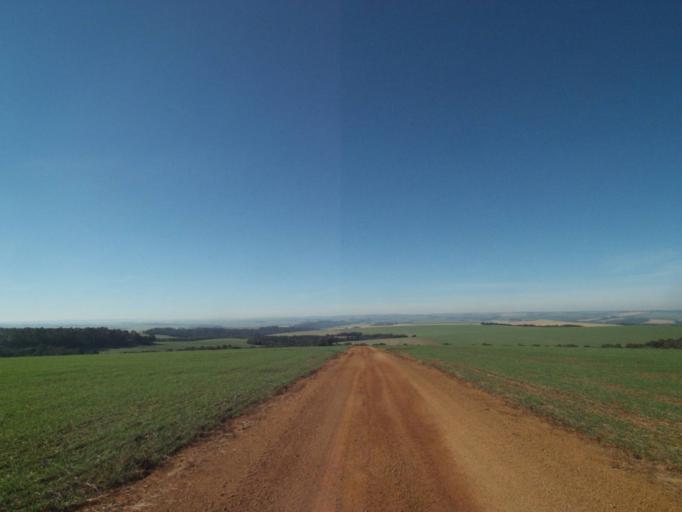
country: BR
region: Parana
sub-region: Tibagi
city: Tibagi
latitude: -24.3872
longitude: -50.3319
